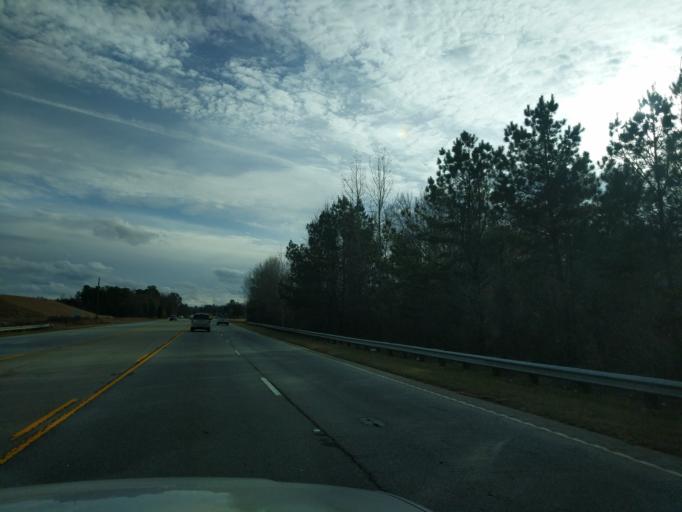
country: US
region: South Carolina
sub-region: Anderson County
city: Honea Path
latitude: 34.5357
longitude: -82.3161
